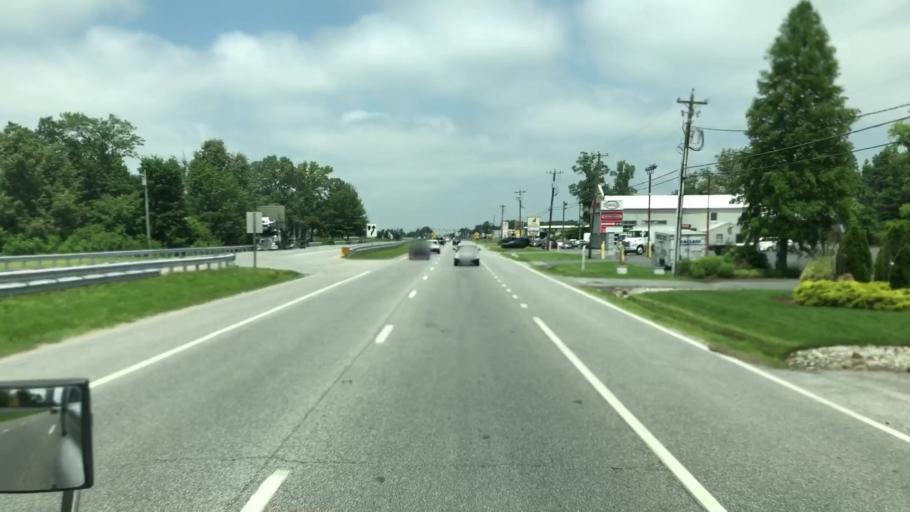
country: US
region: Maryland
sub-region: Talbot County
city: Easton
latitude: 38.8071
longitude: -76.0600
